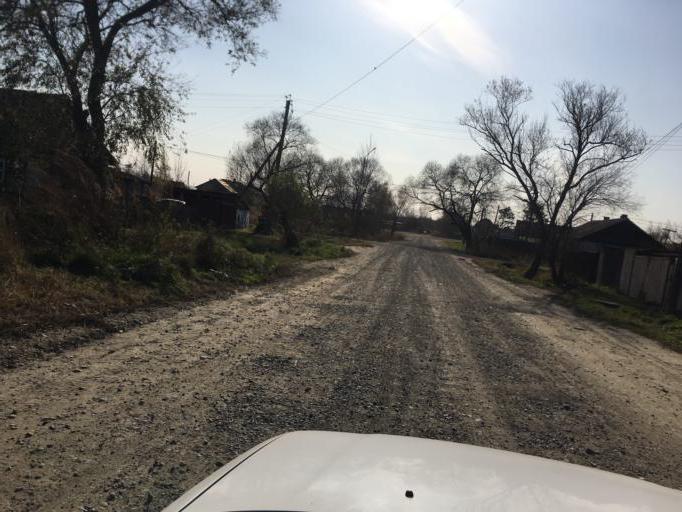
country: RU
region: Primorskiy
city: Dal'nerechensk
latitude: 45.9198
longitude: 133.7229
